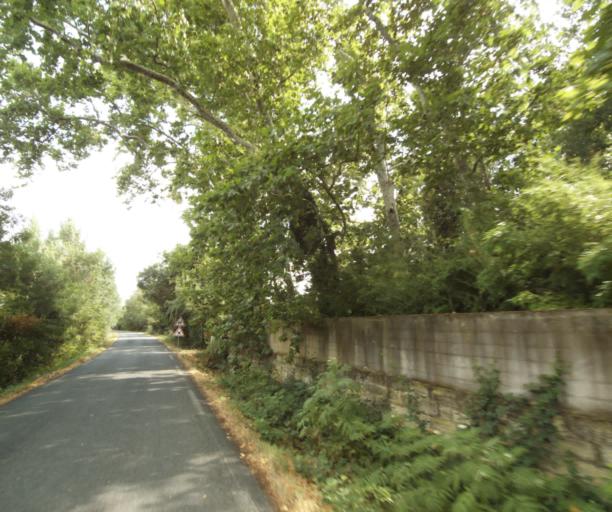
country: FR
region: Languedoc-Roussillon
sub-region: Departement de l'Herault
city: Marsillargues
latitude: 43.6329
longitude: 4.1706
